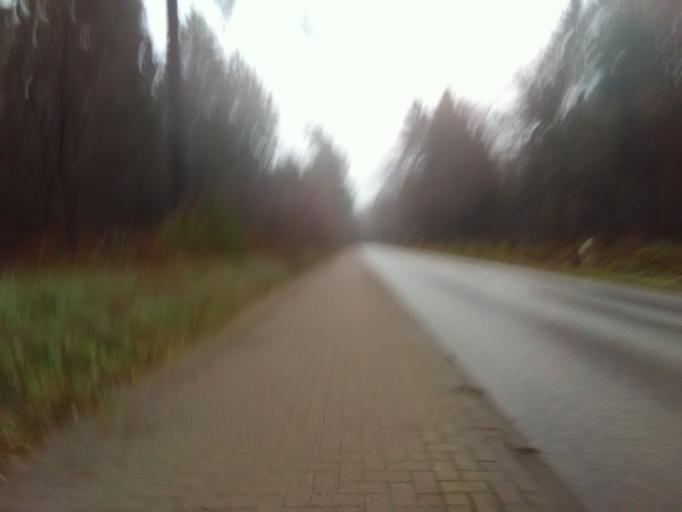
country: DE
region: Schleswig-Holstein
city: Norderstedt
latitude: 53.7204
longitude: 9.9718
